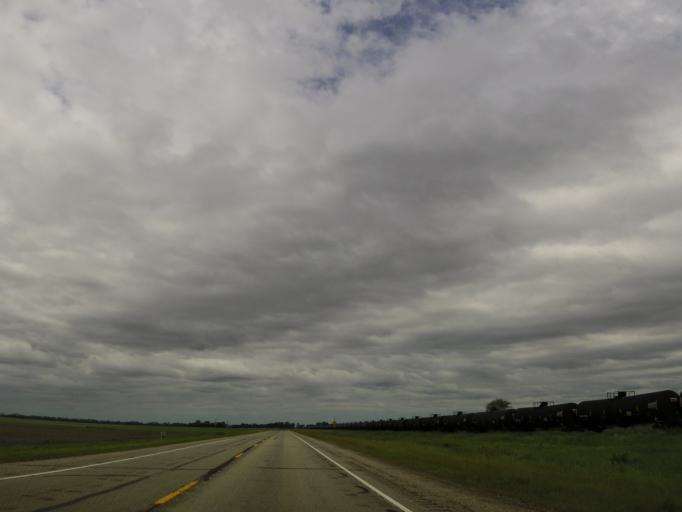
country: US
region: North Dakota
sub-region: Walsh County
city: Grafton
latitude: 48.4903
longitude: -97.4329
